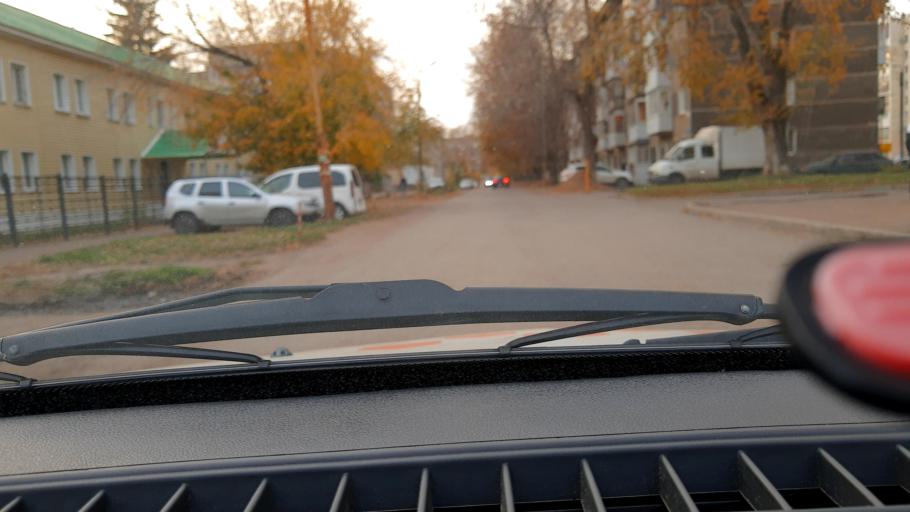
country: RU
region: Bashkortostan
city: Ufa
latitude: 54.8167
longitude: 56.1197
